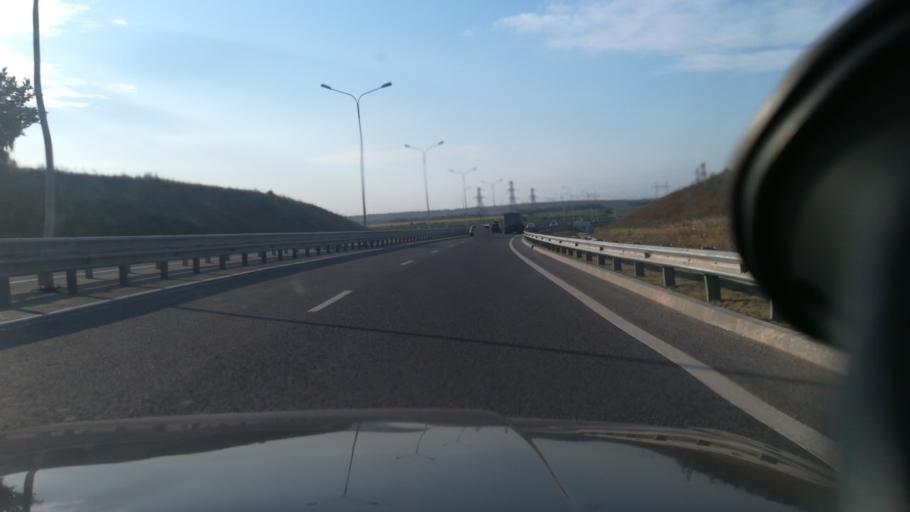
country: RU
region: Krasnodarskiy
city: Dzhiginka
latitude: 45.1240
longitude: 37.3120
